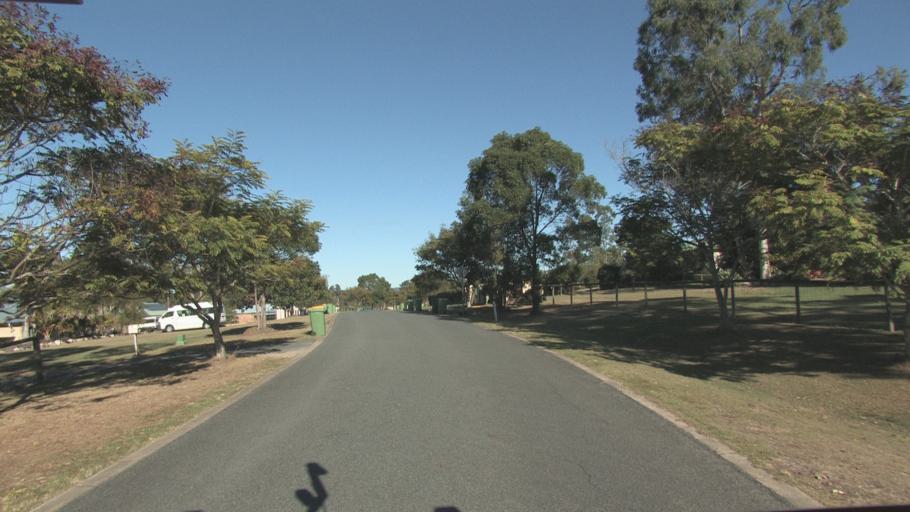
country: AU
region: Queensland
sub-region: Logan
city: North Maclean
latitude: -27.7418
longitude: 152.9618
